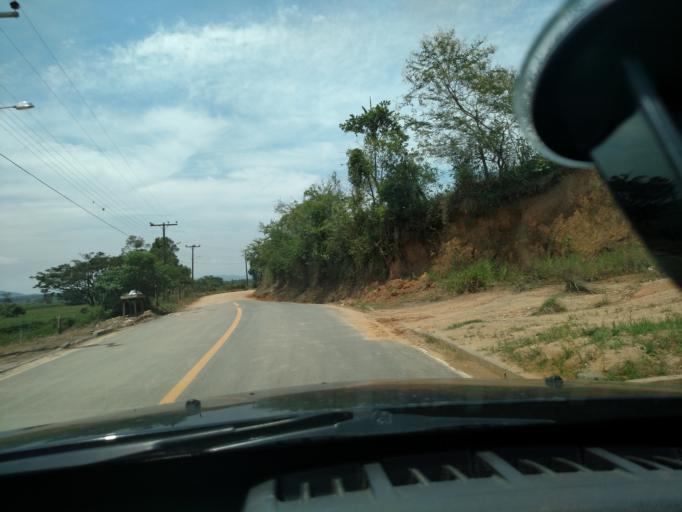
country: BR
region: Santa Catarina
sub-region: Gaspar
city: Gaspar
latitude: -26.9133
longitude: -48.8112
